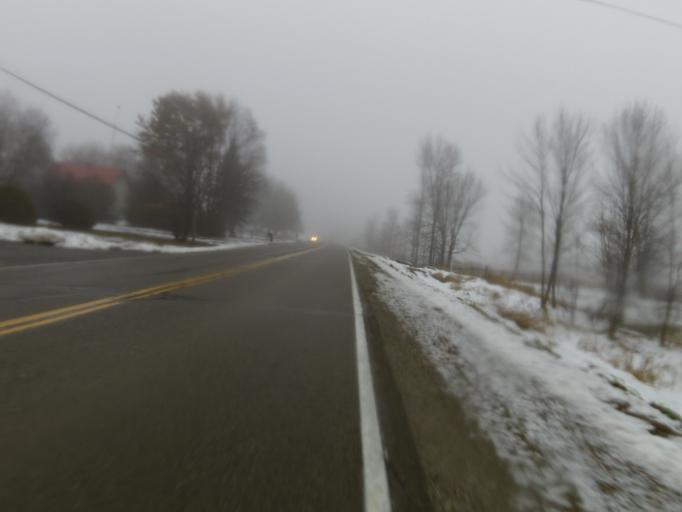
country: CA
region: Ontario
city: Perth
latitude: 44.8469
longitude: -76.3599
